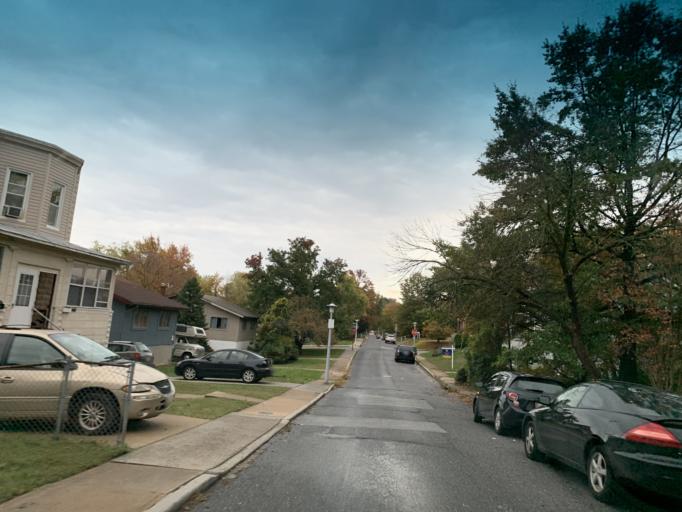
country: US
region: Maryland
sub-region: Baltimore County
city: Rosedale
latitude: 39.3328
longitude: -76.5535
